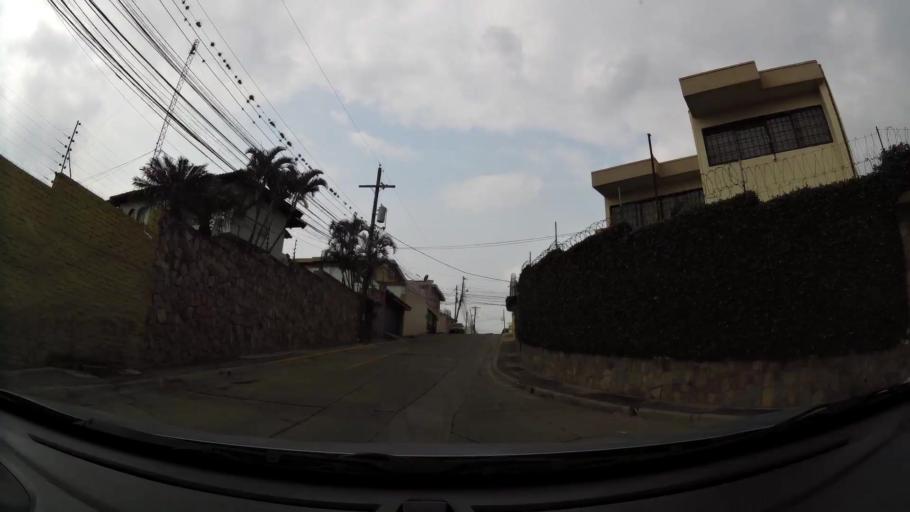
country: HN
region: Francisco Morazan
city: Tegucigalpa
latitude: 14.0934
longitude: -87.1841
